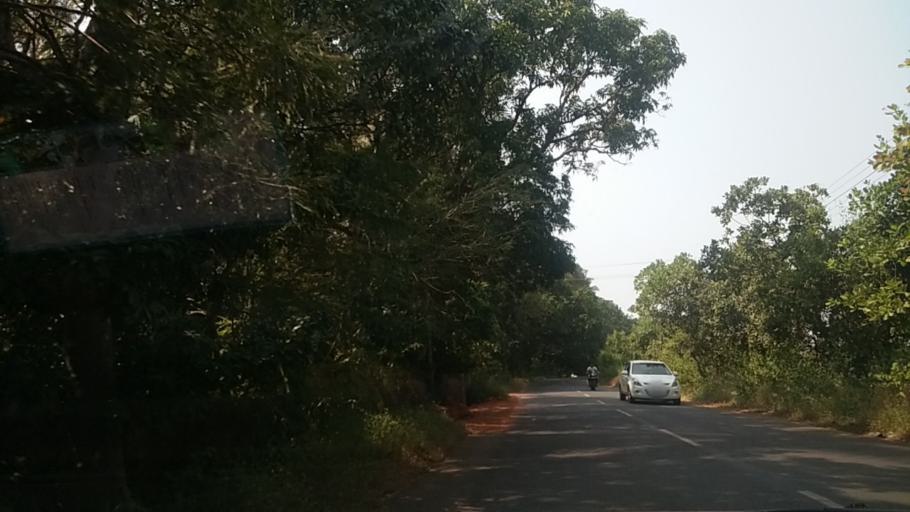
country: IN
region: Goa
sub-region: North Goa
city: Morjim
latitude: 15.6626
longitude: 73.7290
